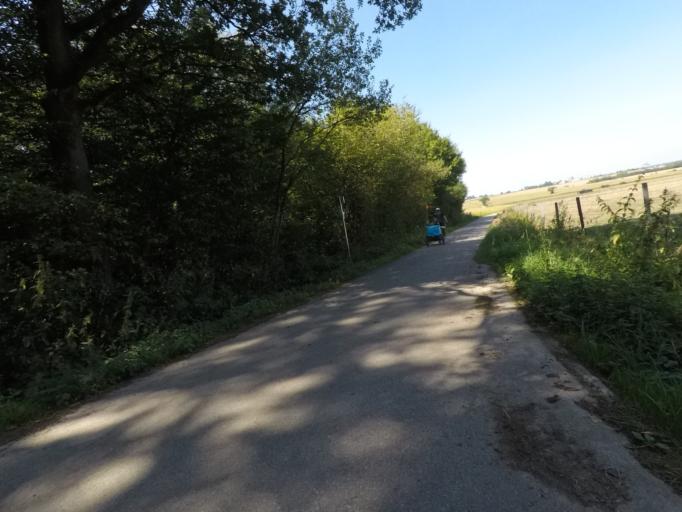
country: LU
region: Luxembourg
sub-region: Canton de Capellen
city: Garnich
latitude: 49.6310
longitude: 5.9340
